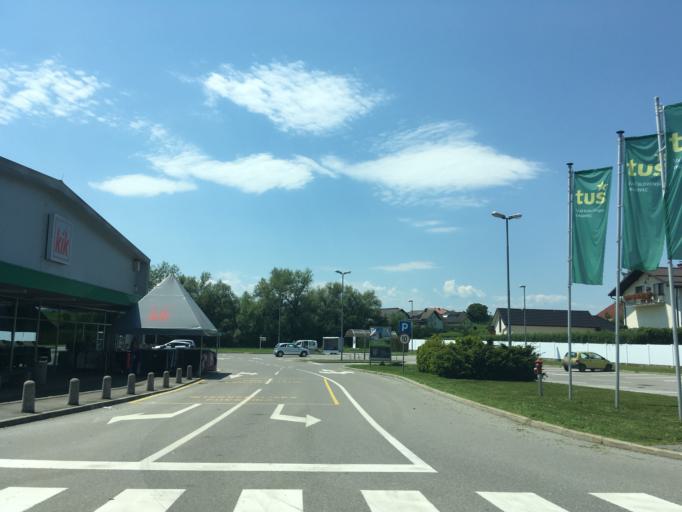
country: SI
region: Metlika
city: Metlika
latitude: 45.6387
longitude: 15.3217
